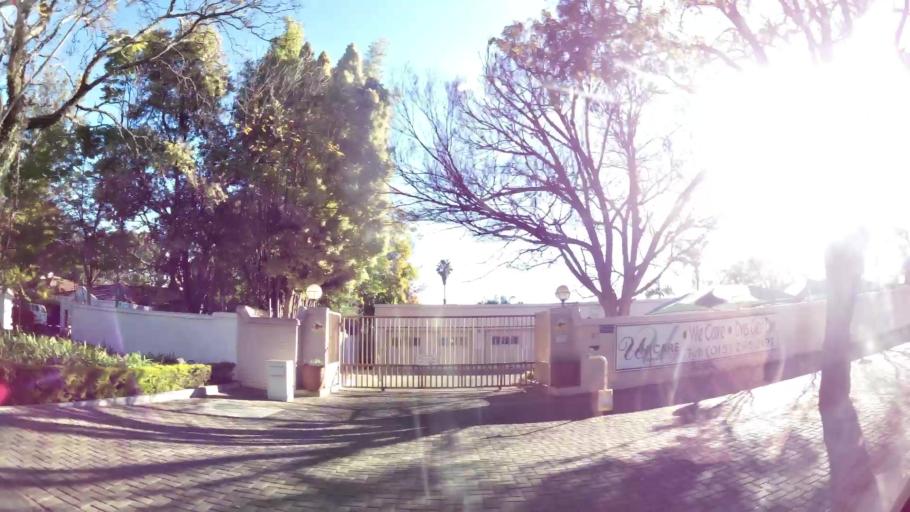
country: ZA
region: Limpopo
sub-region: Capricorn District Municipality
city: Polokwane
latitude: -23.9060
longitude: 29.4627
